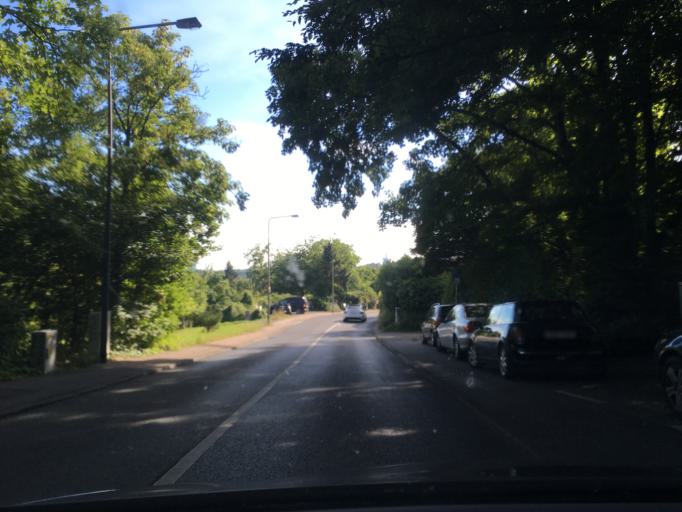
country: DE
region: Hesse
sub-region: Regierungsbezirk Darmstadt
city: Bad Vilbel
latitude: 50.1486
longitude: 8.7355
